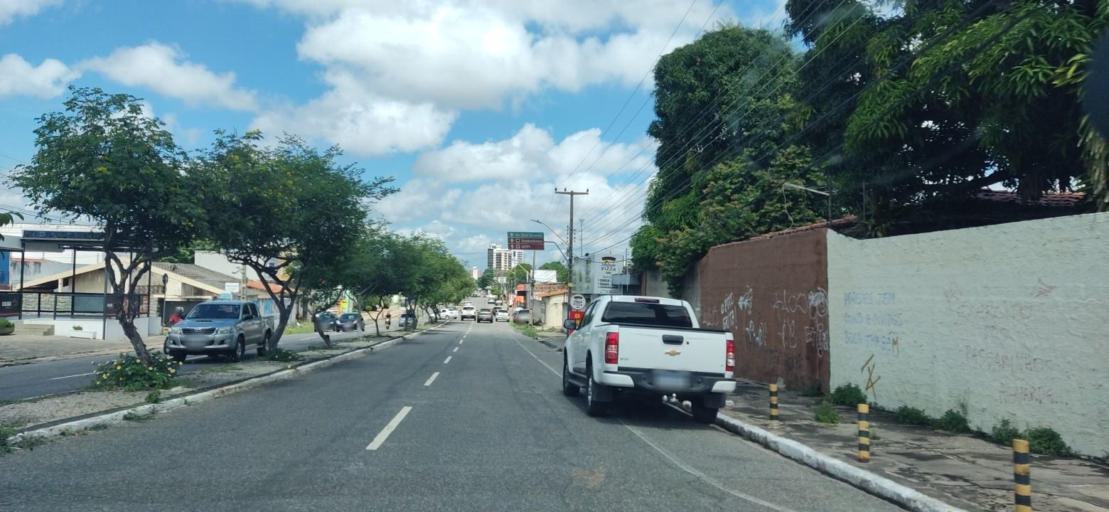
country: BR
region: Piaui
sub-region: Teresina
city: Teresina
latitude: -5.0708
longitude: -42.7651
